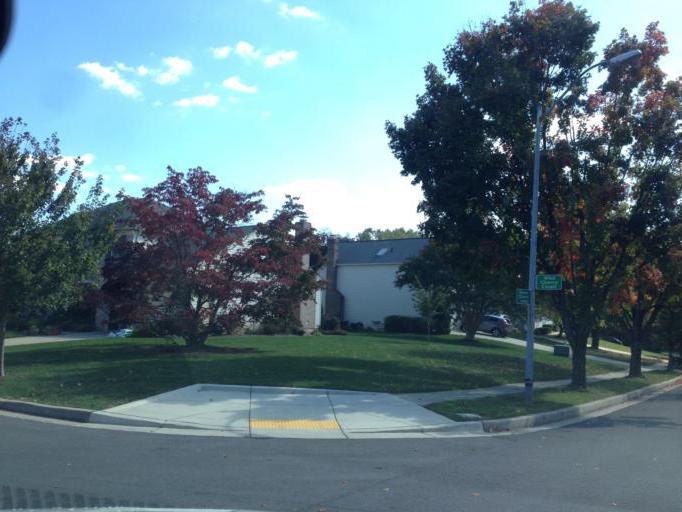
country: US
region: Maryland
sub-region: Howard County
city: North Laurel
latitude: 39.1397
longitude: -76.8951
